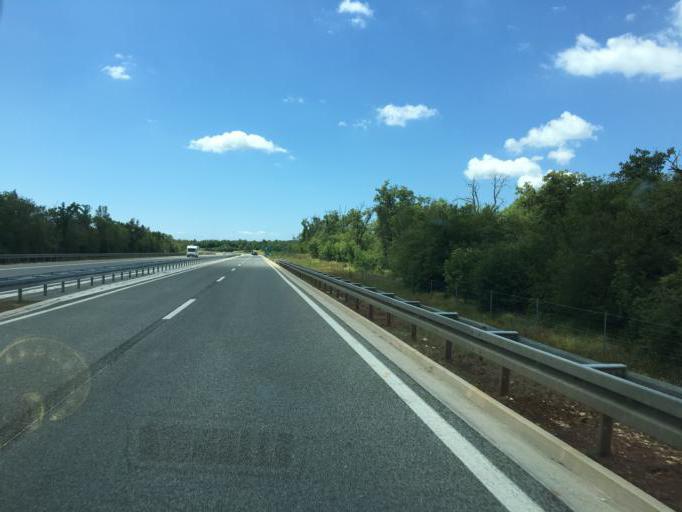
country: HR
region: Istarska
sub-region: Grad Rovinj
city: Rovinj
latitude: 45.1673
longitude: 13.7307
